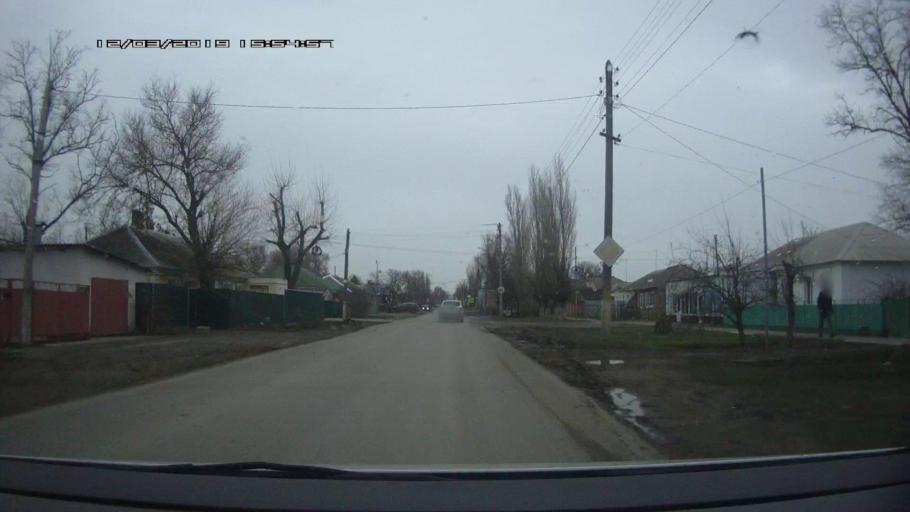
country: RU
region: Rostov
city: Novobataysk
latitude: 46.8938
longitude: 39.7787
